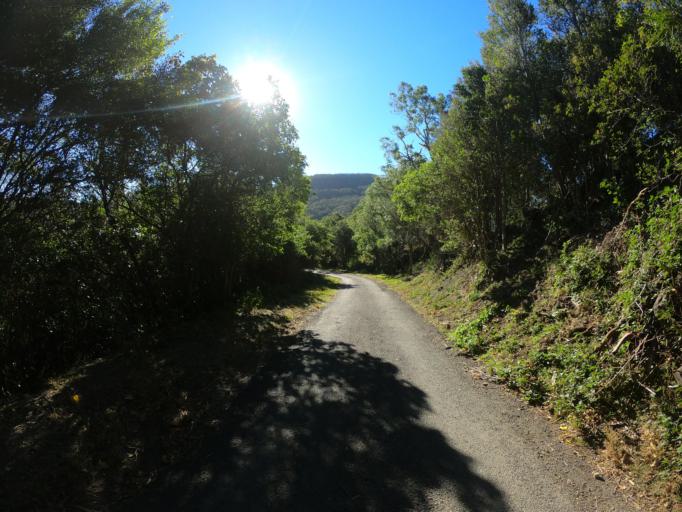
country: AU
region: New South Wales
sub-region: Wollongong
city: Mount Keira
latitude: -34.4193
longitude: 150.8393
